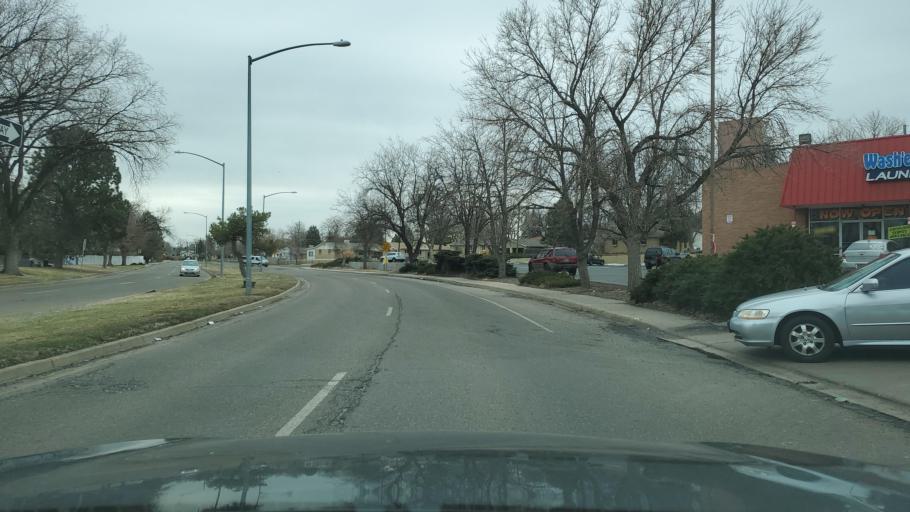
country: US
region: Colorado
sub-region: Adams County
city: Aurora
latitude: 39.7318
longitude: -104.8647
